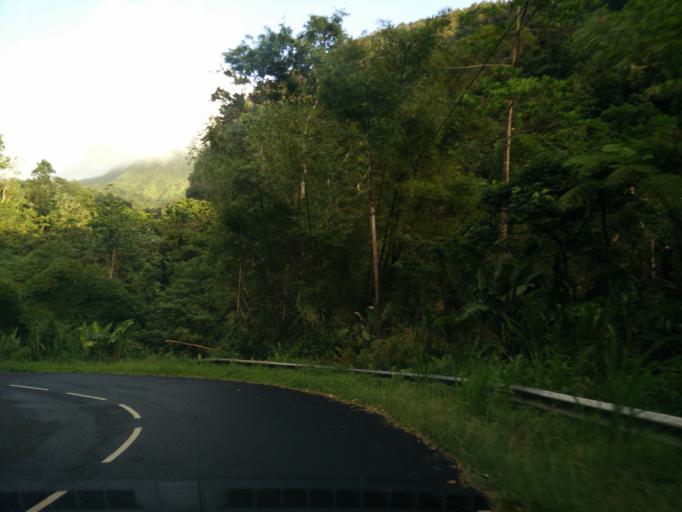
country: MQ
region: Martinique
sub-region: Martinique
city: Le Morne-Rouge
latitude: 14.7306
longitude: -61.1210
